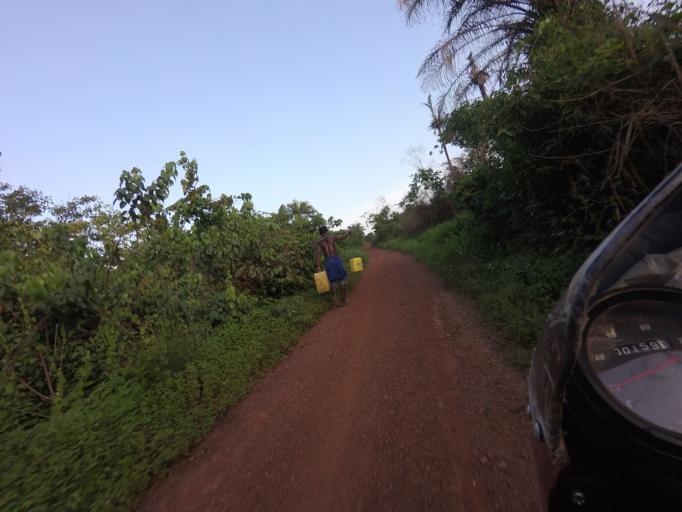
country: SL
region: Eastern Province
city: Tombu
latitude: 8.4044
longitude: -10.7120
